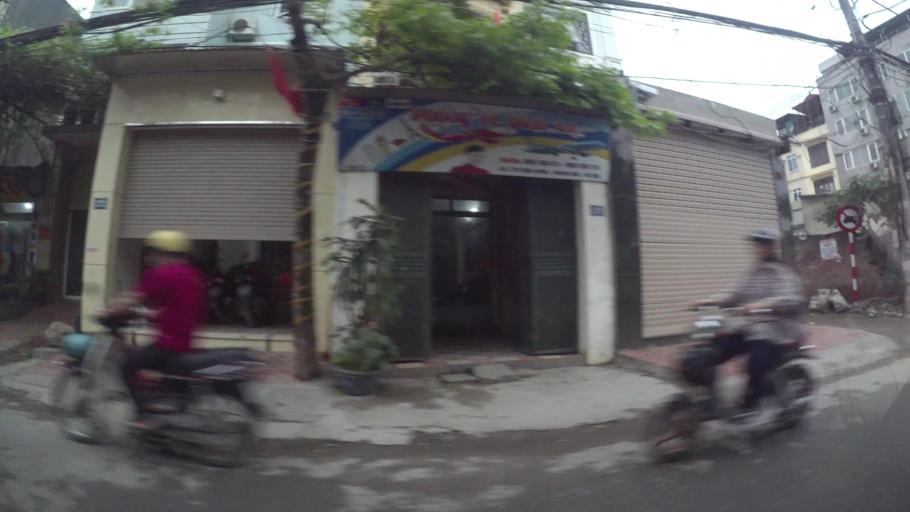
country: VN
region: Ha Noi
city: Hai BaTrung
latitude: 20.9922
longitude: 105.8795
